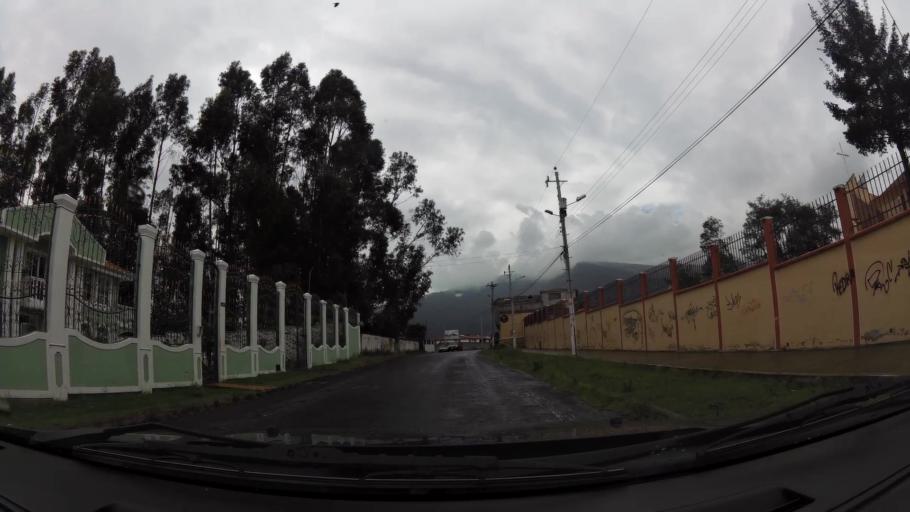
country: EC
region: Pichincha
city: Sangolqui
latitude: -0.2963
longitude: -78.4444
